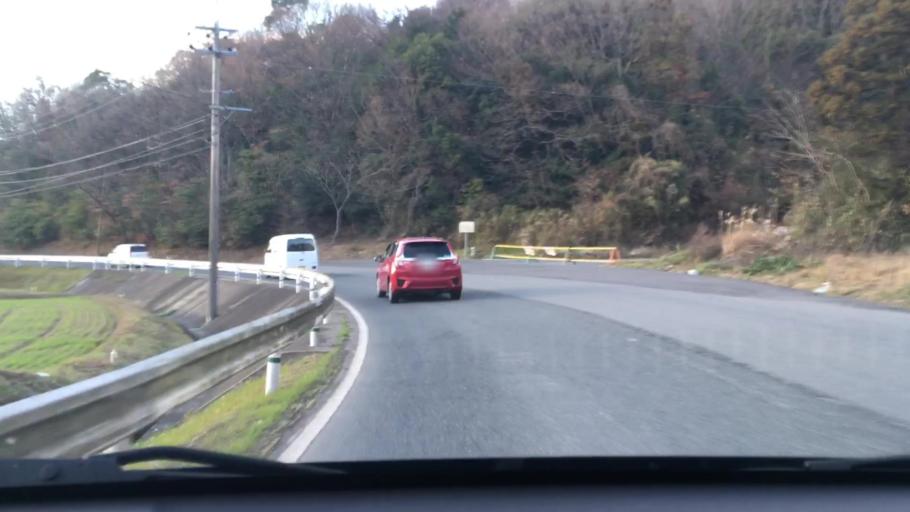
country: JP
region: Oita
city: Bungo-Takada-shi
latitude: 33.5076
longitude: 131.3614
